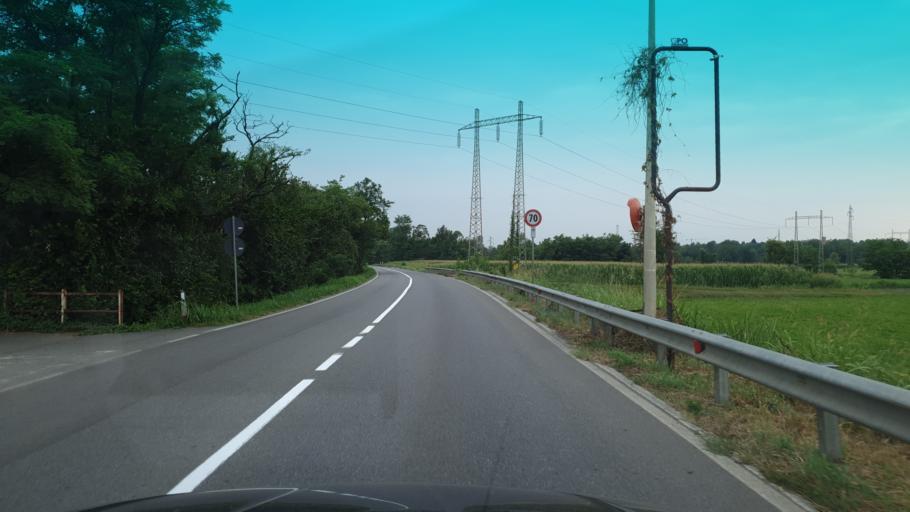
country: IT
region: Lombardy
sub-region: Provincia di Bergamo
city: Fara Gera d'Adda
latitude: 45.5456
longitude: 9.5366
